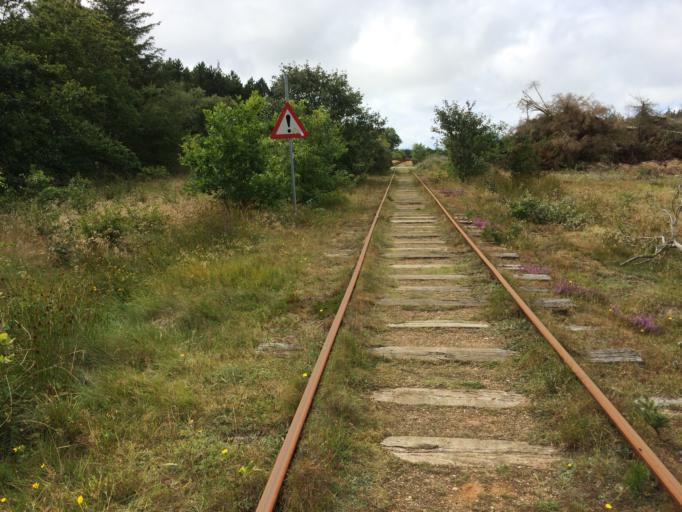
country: DK
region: South Denmark
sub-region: Varde Kommune
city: Oksbol
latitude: 55.7865
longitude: 8.2409
